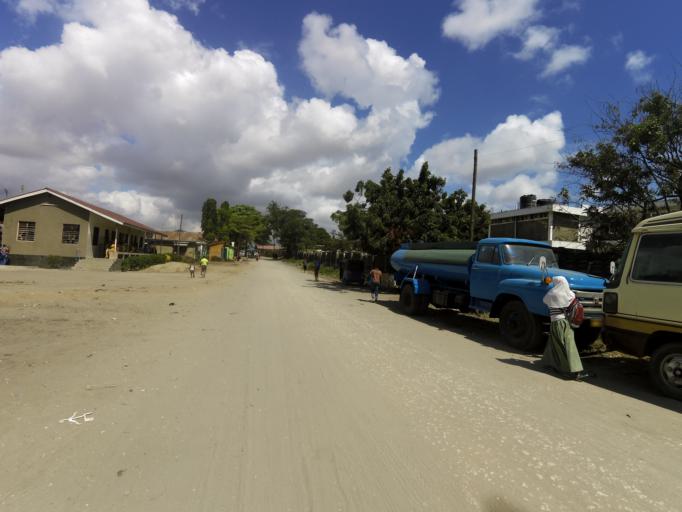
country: TZ
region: Dar es Salaam
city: Magomeni
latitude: -6.7885
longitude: 39.2548
